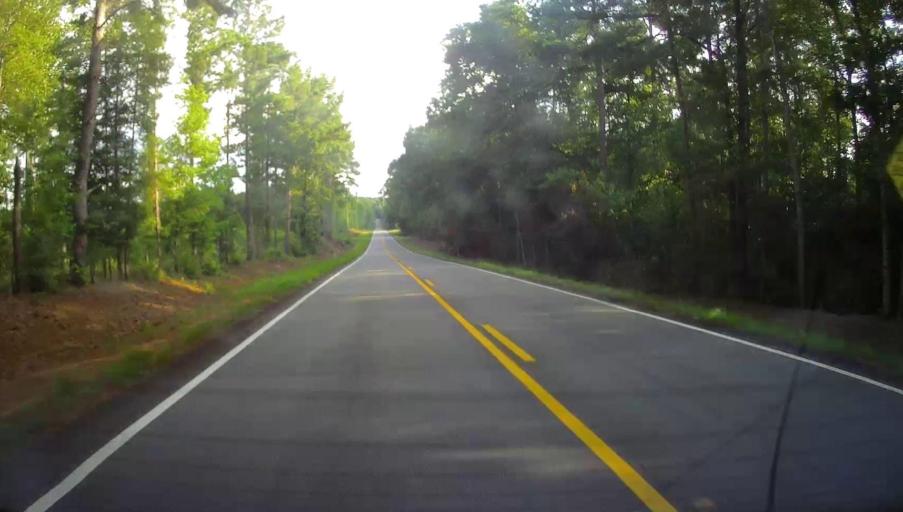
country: US
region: Georgia
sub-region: Monroe County
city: Forsyth
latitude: 32.8915
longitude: -83.9943
